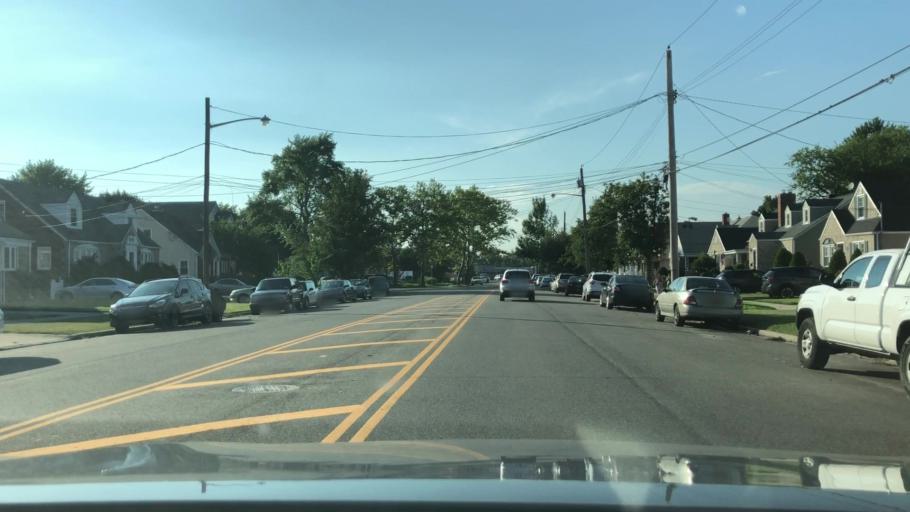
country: US
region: New York
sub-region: Nassau County
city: North New Hyde Park
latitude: 40.7391
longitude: -73.6961
